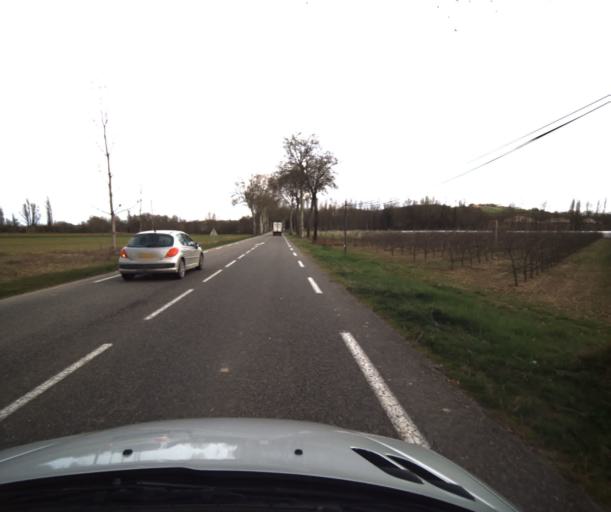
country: FR
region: Midi-Pyrenees
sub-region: Departement du Tarn-et-Garonne
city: Moissac
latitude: 44.1285
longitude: 1.1612
